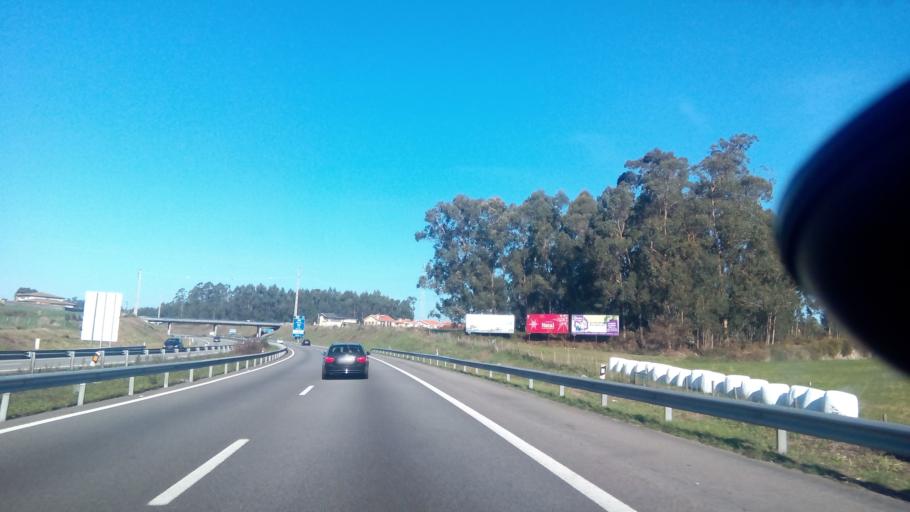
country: PT
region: Porto
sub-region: Matosinhos
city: Lavra
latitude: 41.2793
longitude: -8.6989
